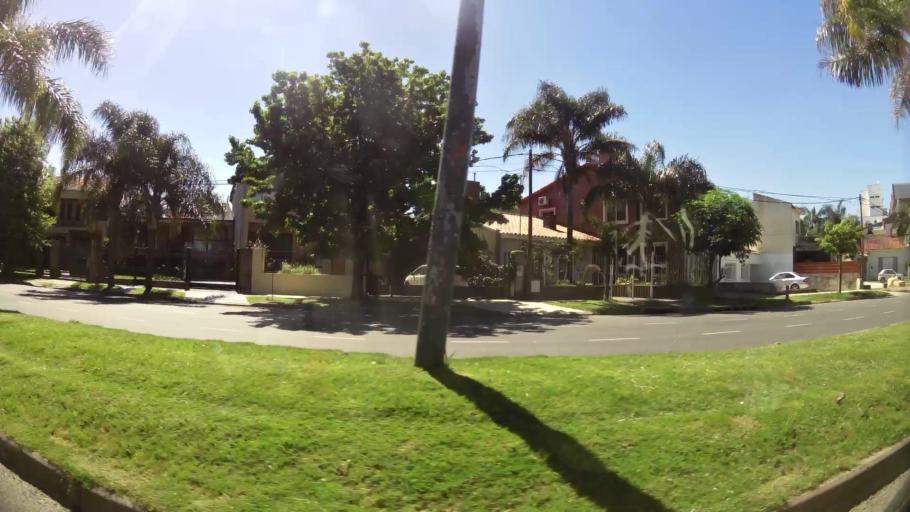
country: AR
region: Santa Fe
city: Santa Fe de la Vera Cruz
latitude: -31.6184
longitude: -60.6760
